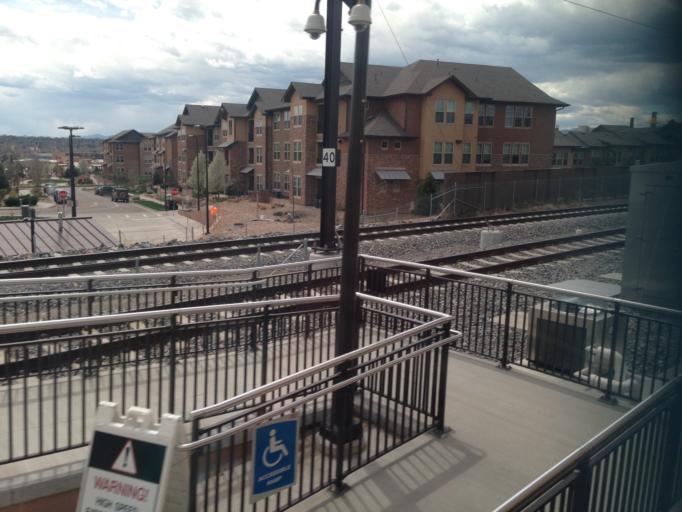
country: US
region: Colorado
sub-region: Jefferson County
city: Arvada
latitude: 39.7924
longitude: -105.1121
